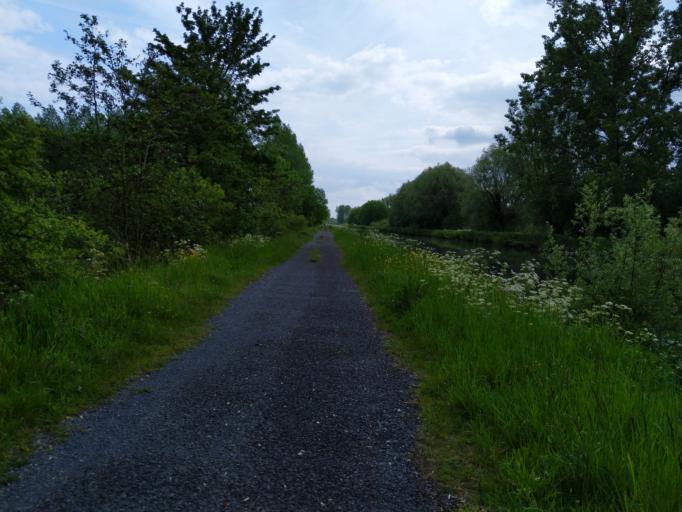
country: FR
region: Nord-Pas-de-Calais
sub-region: Departement du Nord
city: Landrecies
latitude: 50.0735
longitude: 3.6477
